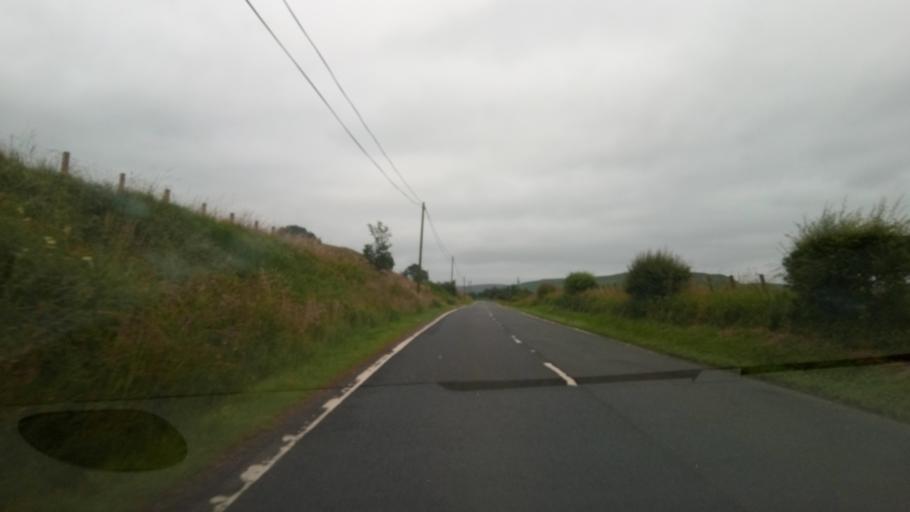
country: GB
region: Scotland
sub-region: The Scottish Borders
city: Hawick
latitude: 55.3448
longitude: -2.9264
